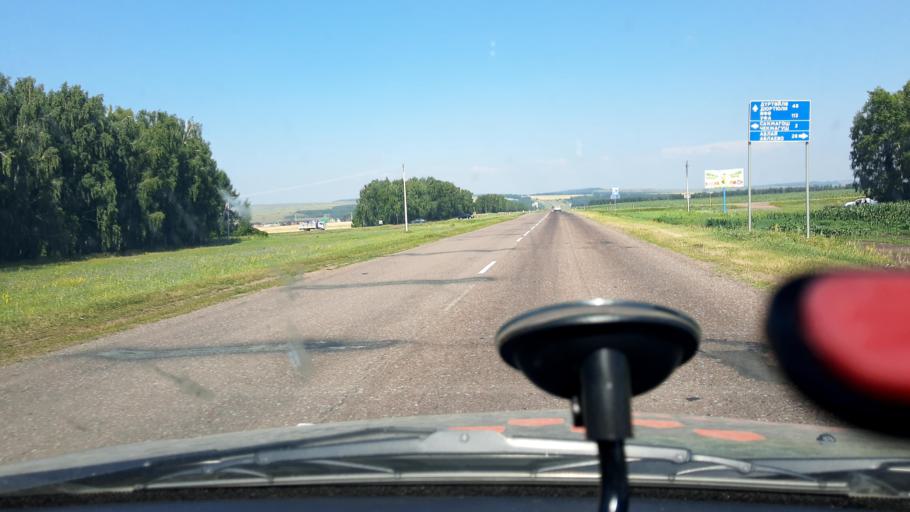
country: RU
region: Bashkortostan
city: Chekmagush
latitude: 55.1172
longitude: 54.6628
